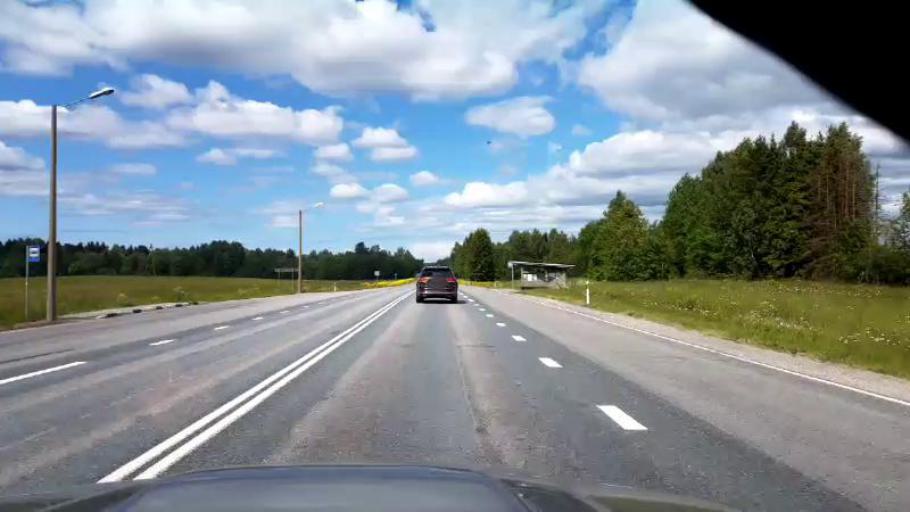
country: EE
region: Harju
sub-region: Saue linn
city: Saue
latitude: 59.1565
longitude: 24.5050
